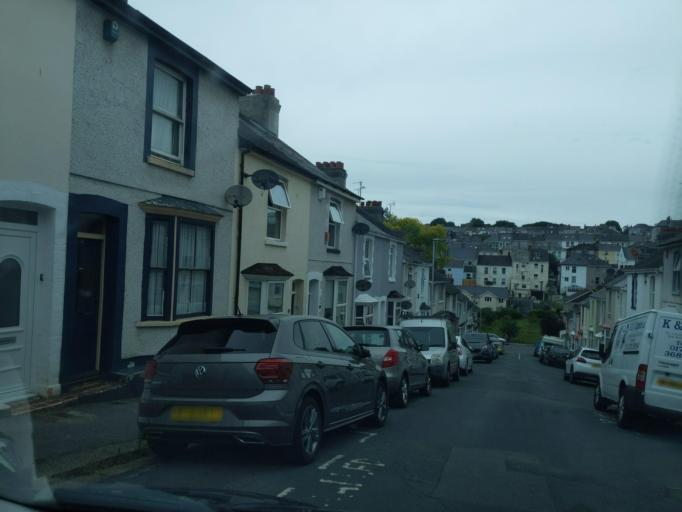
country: GB
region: England
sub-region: Cornwall
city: Millbrook
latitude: 50.3837
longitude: -4.1681
